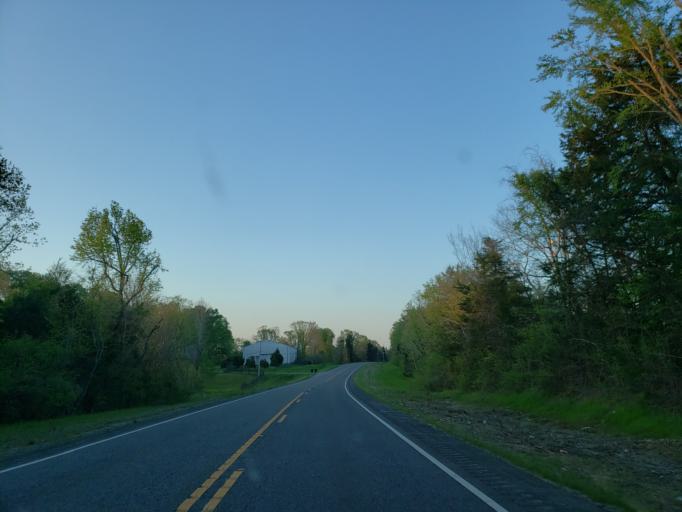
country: US
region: Alabama
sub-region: Sumter County
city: Livingston
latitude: 32.6462
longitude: -88.1715
